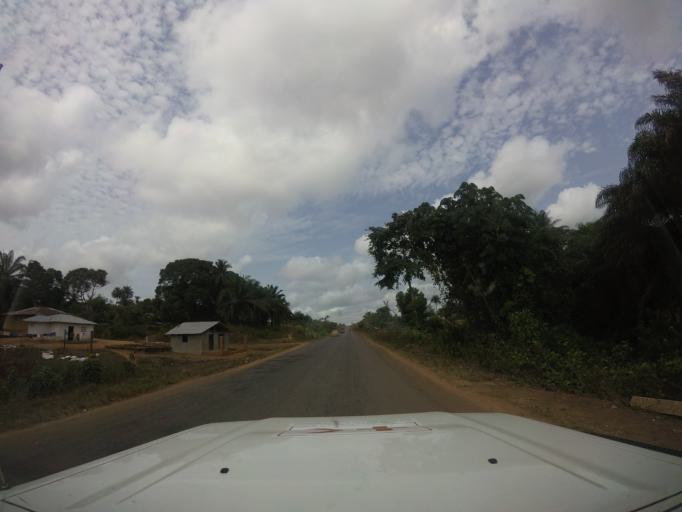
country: LR
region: Bomi
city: Tubmanburg
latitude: 6.7290
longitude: -11.0233
